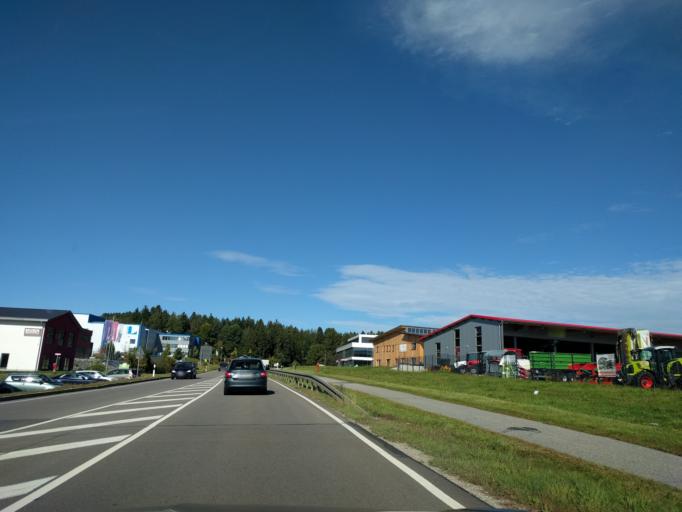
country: DE
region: Bavaria
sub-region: Lower Bavaria
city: Patersdorf
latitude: 49.0261
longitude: 12.9710
